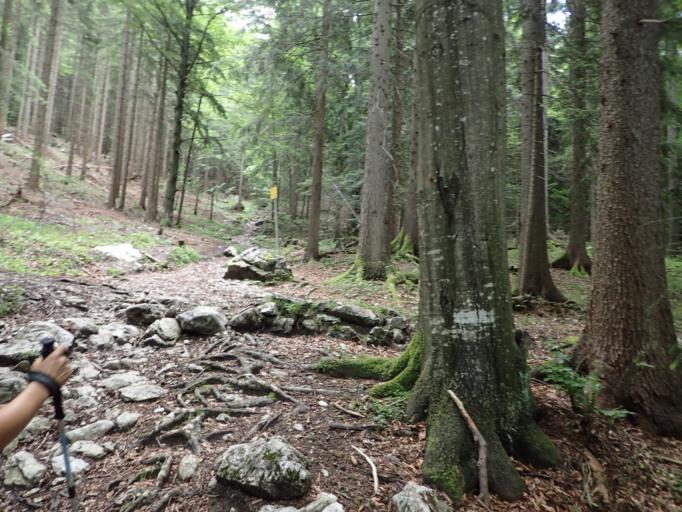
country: AT
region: Salzburg
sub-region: Politischer Bezirk Salzburg-Umgebung
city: Fuschl am See
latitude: 47.8124
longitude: 13.3054
